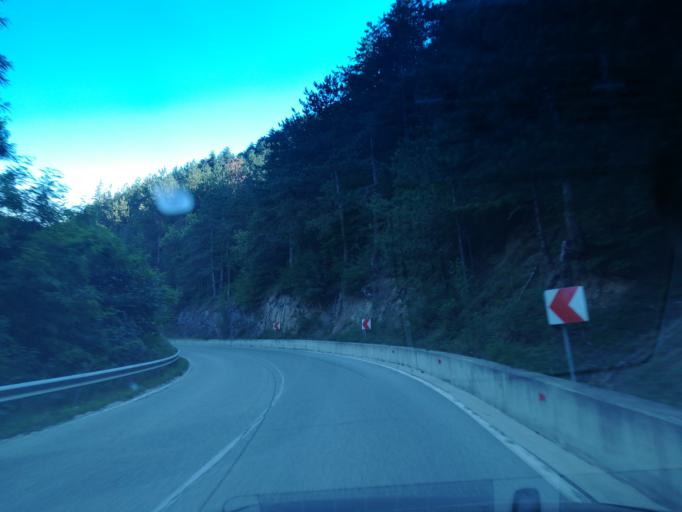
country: BG
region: Smolyan
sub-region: Obshtina Chepelare
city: Chepelare
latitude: 41.8481
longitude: 24.6804
